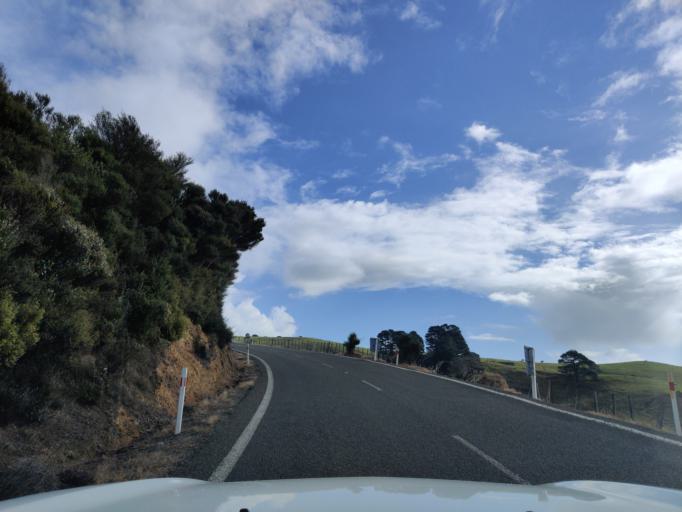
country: NZ
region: Waikato
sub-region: Thames-Coromandel District
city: Coromandel
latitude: -36.8145
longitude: 175.4883
